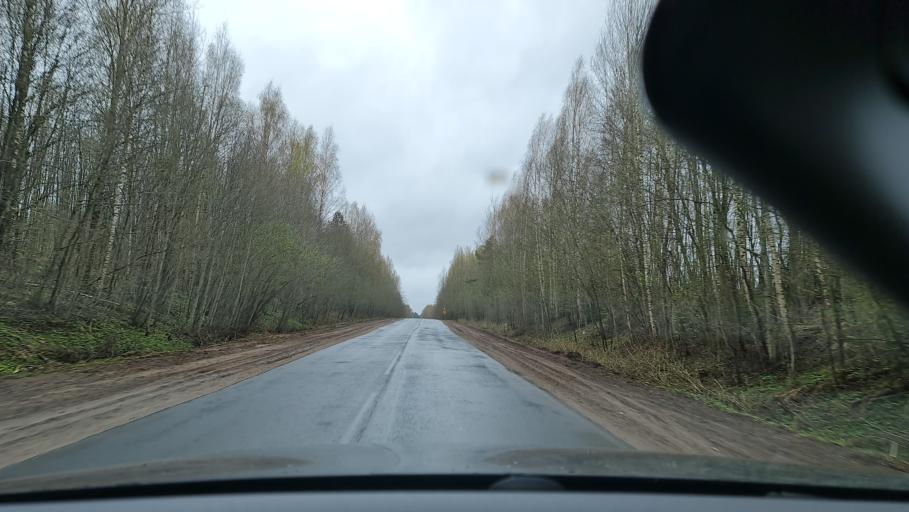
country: RU
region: Novgorod
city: Demyansk
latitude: 57.7398
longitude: 32.5733
